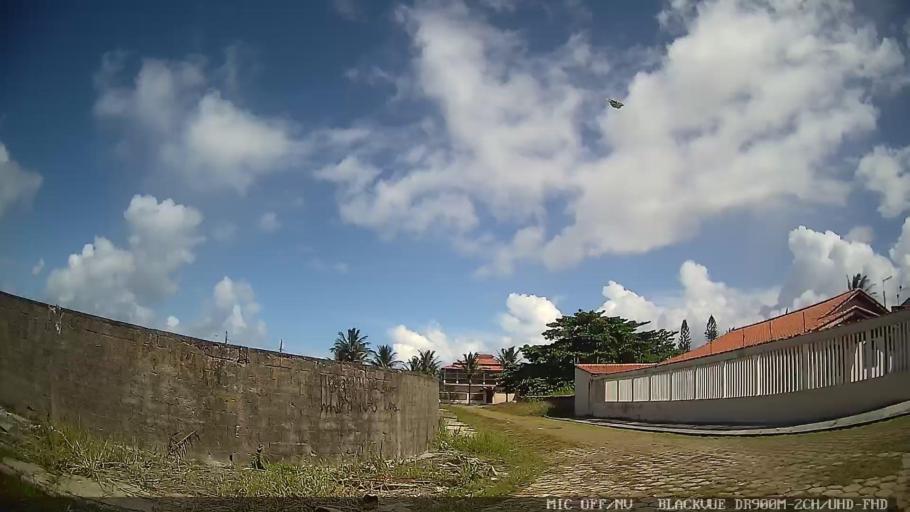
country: BR
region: Sao Paulo
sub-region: Itanhaem
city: Itanhaem
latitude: -24.2305
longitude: -46.8676
